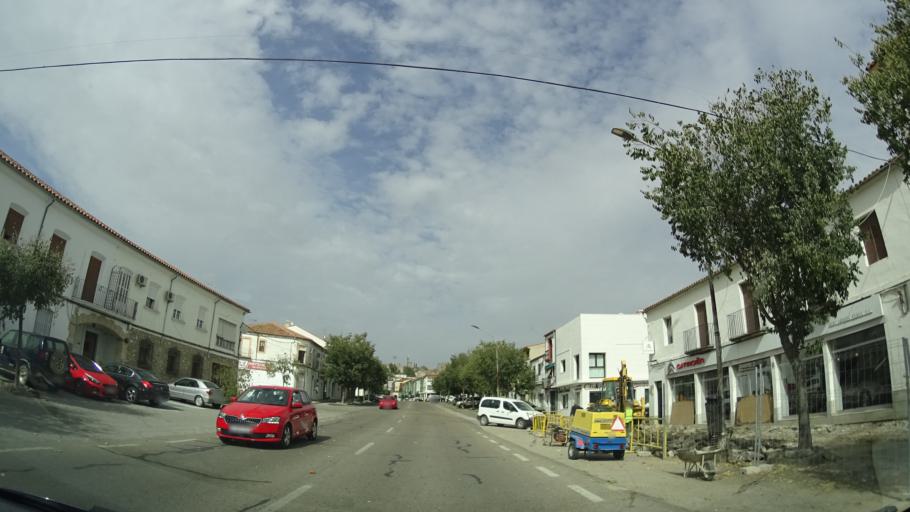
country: ES
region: Extremadura
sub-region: Provincia de Caceres
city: Trujillo
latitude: 39.4544
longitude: -5.8806
